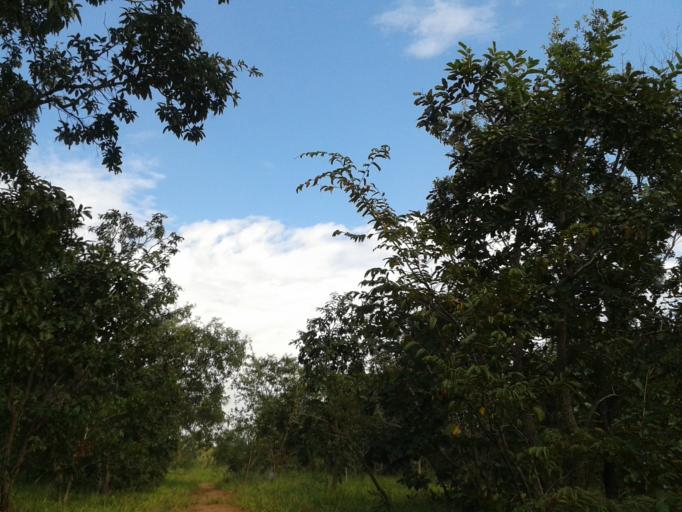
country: BR
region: Minas Gerais
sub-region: Campina Verde
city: Campina Verde
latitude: -19.3946
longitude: -49.6516
